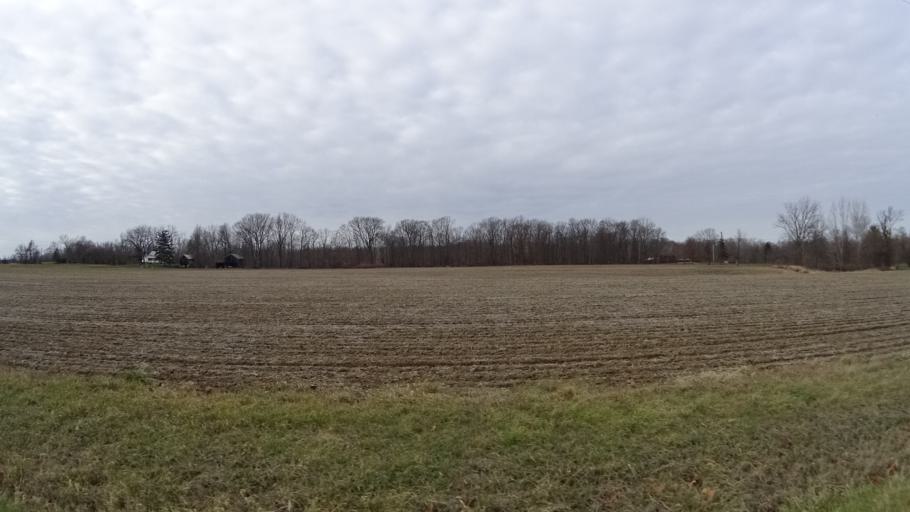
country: US
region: Ohio
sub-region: Lorain County
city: Wellington
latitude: 41.1761
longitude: -82.2688
